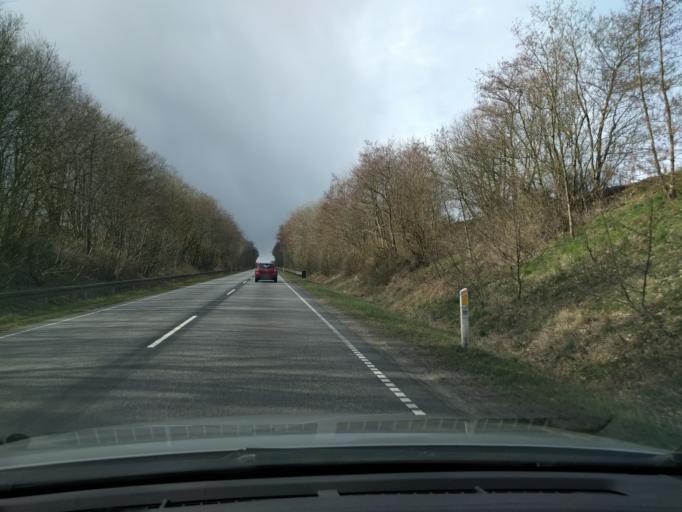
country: DK
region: South Denmark
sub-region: Kolding Kommune
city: Vamdrup
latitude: 55.4260
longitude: 9.2813
